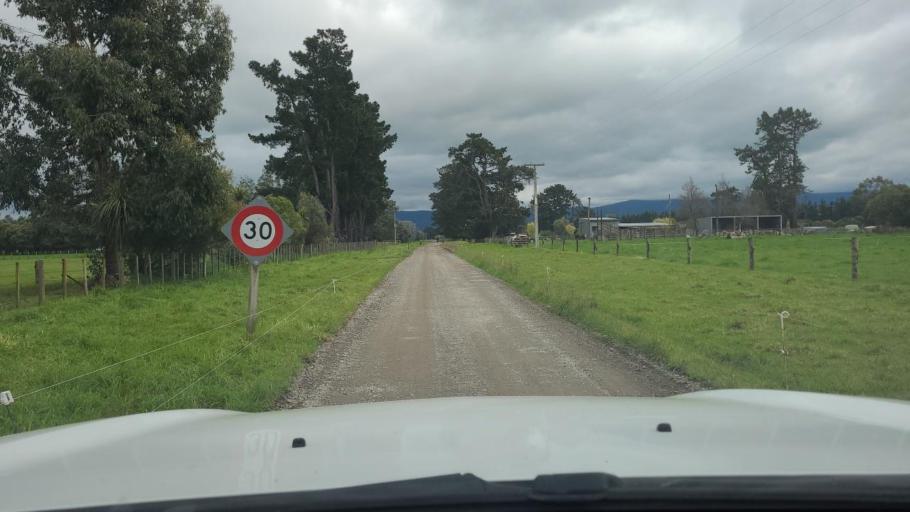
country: NZ
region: Wellington
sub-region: Masterton District
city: Masterton
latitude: -41.1285
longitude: 175.4279
